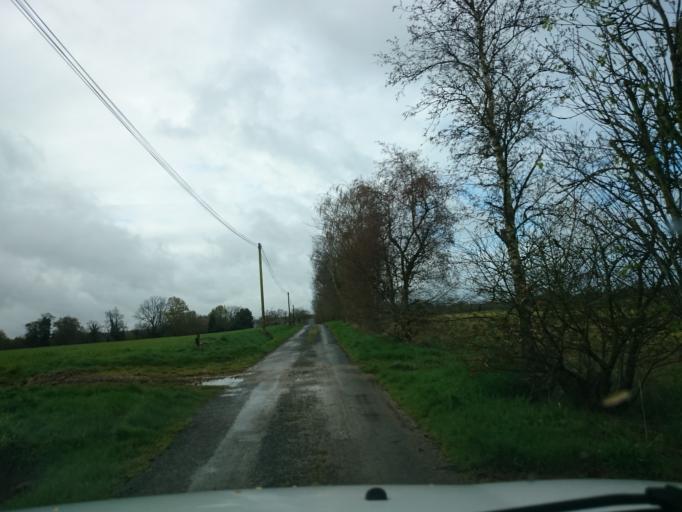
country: FR
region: Brittany
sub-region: Departement d'Ille-et-Vilaine
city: Fouillard
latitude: 48.1387
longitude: -1.5633
